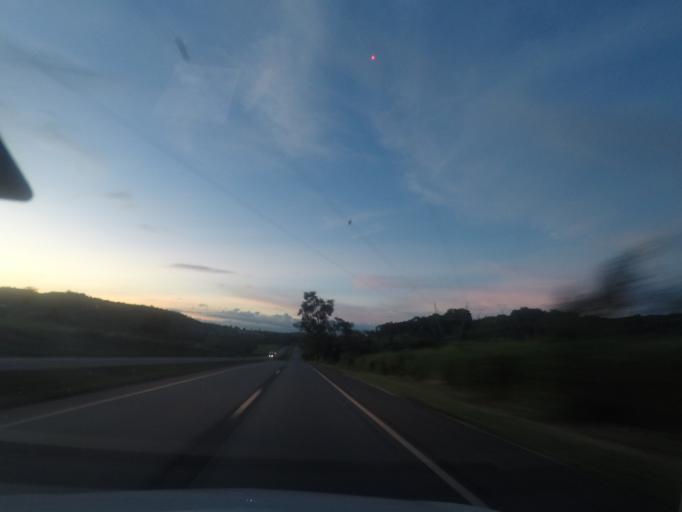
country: BR
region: Goias
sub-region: Pontalina
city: Pontalina
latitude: -17.4540
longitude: -49.2254
